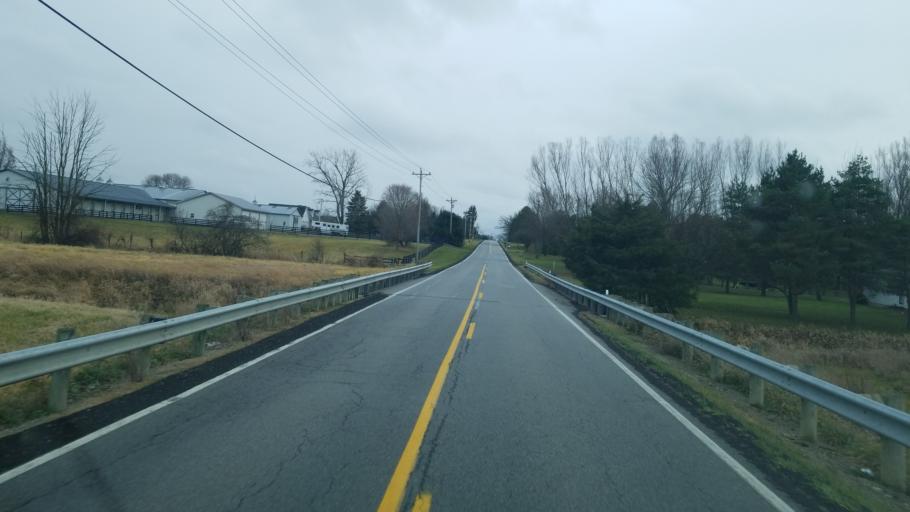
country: US
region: Ohio
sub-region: Union County
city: Marysville
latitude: 40.3234
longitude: -83.3543
